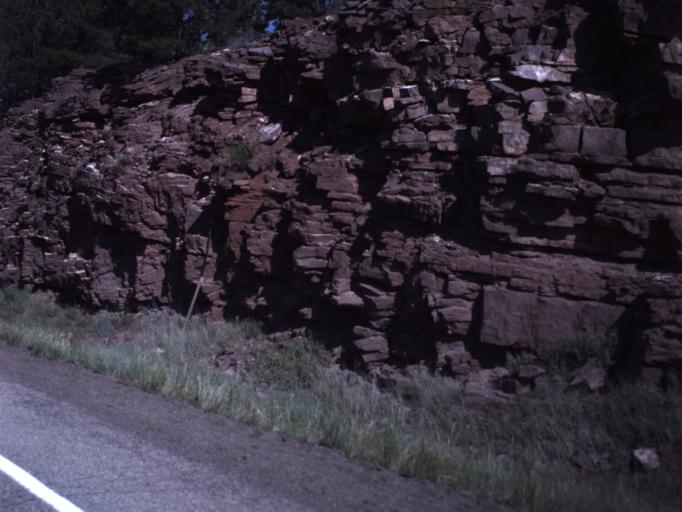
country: US
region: Utah
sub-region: Daggett County
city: Manila
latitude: 40.8576
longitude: -109.6830
